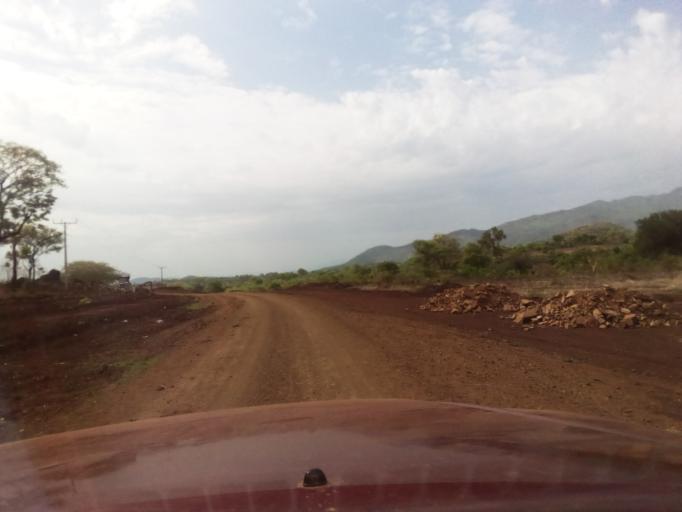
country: ET
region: Oromiya
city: Mendi
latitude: 10.0609
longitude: 35.2806
